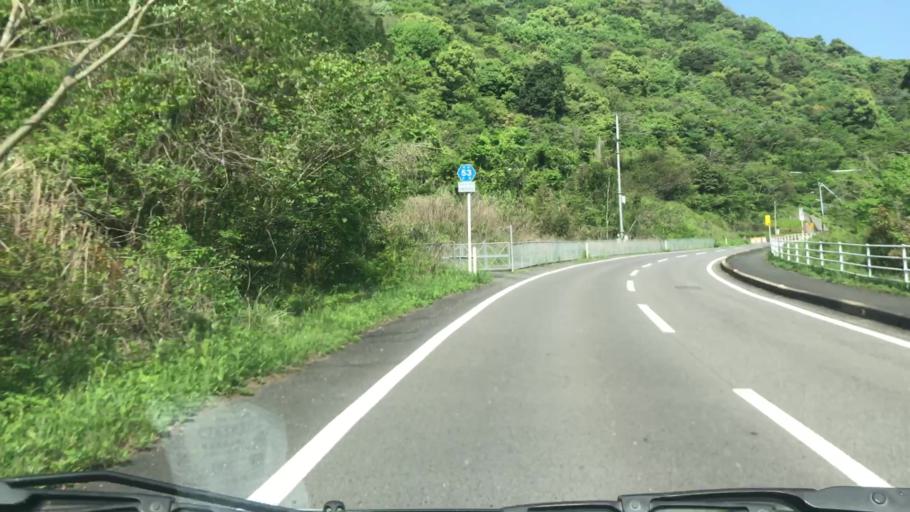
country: JP
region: Saga Prefecture
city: Takeocho-takeo
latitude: 33.2127
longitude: 130.0083
